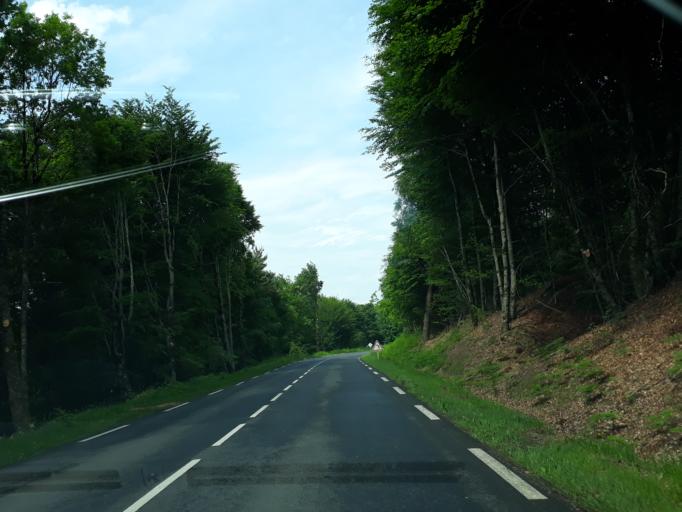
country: FR
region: Limousin
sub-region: Departement de la Correze
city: Beynat
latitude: 45.1212
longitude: 1.7862
